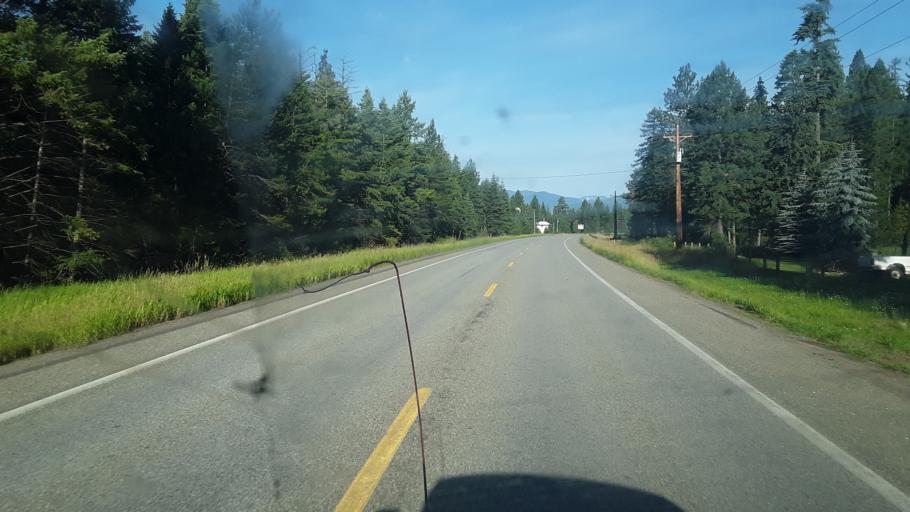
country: US
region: Idaho
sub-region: Boundary County
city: Bonners Ferry
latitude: 48.7267
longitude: -116.2064
